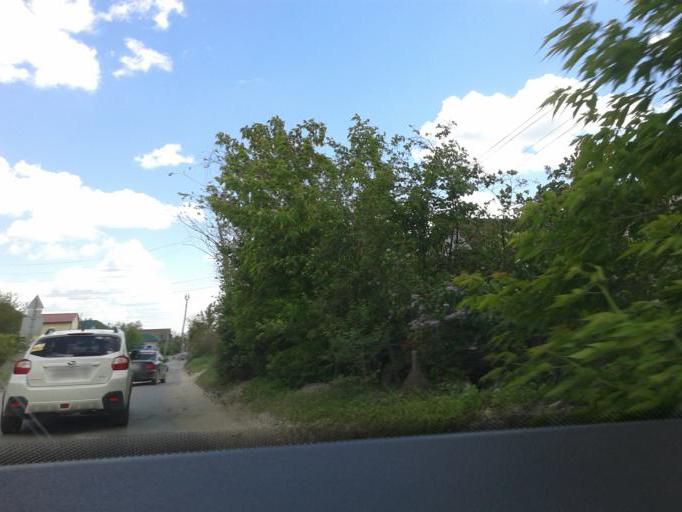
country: RU
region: Volgograd
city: Volgograd
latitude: 48.6937
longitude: 44.4520
